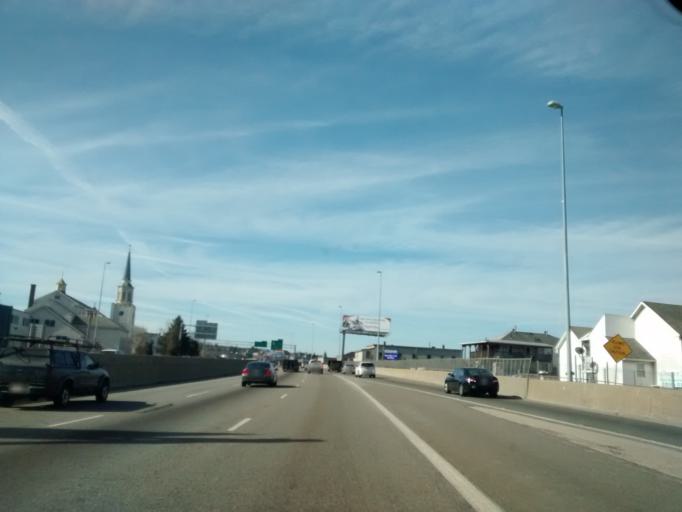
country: US
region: Massachusetts
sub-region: Worcester County
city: Worcester
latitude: 42.2530
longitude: -71.7982
